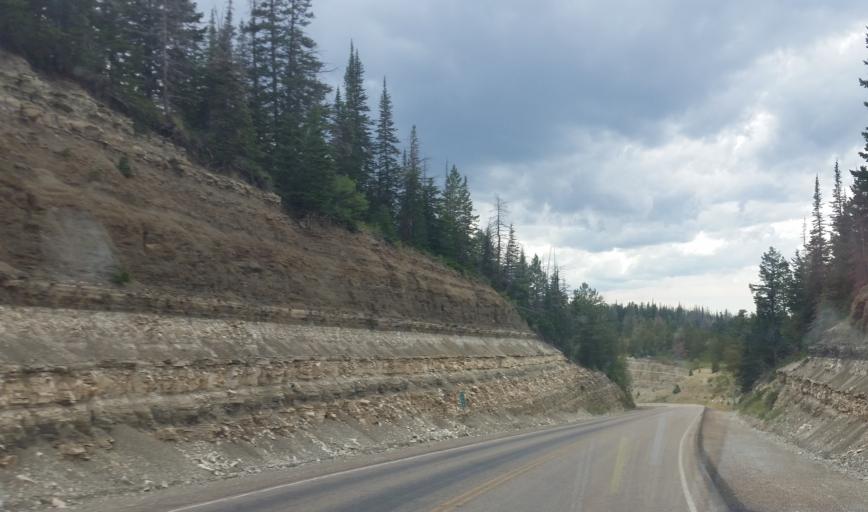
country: US
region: Utah
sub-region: Carbon County
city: Helper
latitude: 39.8778
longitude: -110.7543
